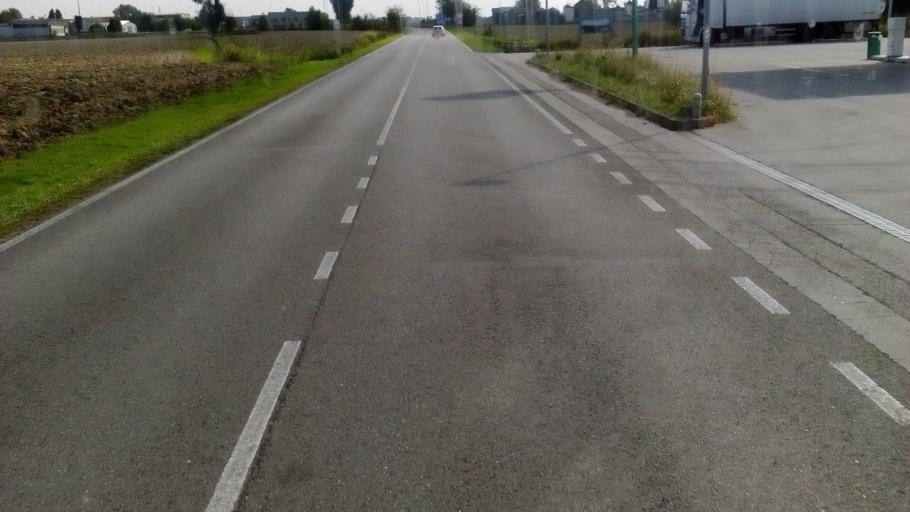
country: IT
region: Veneto
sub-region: Provincia di Rovigo
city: Calto
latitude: 44.9982
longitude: 11.3573
